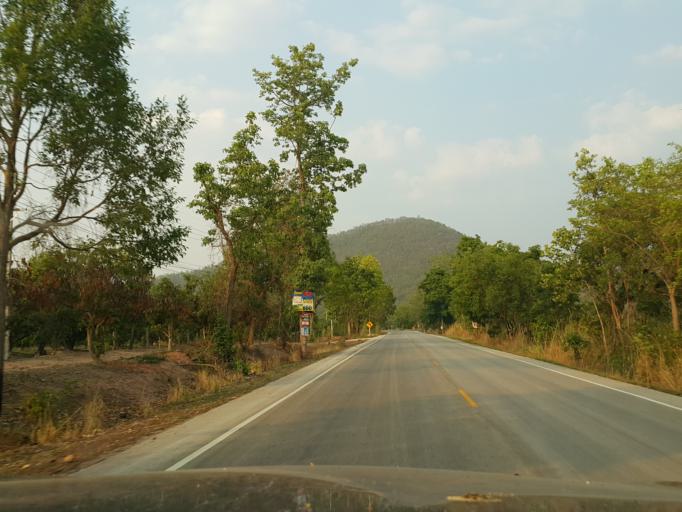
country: TH
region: Lamphun
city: Li
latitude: 17.8296
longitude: 98.9853
